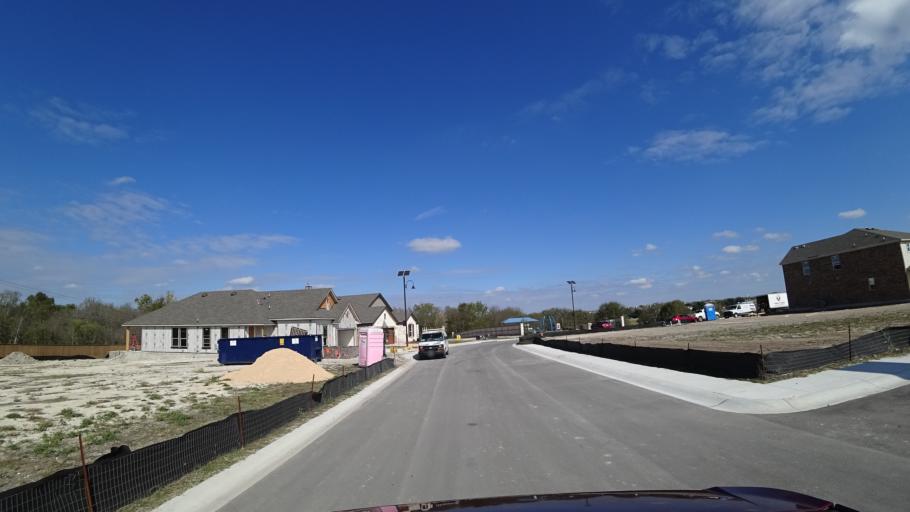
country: US
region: Texas
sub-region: Travis County
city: Windemere
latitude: 30.4523
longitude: -97.6333
